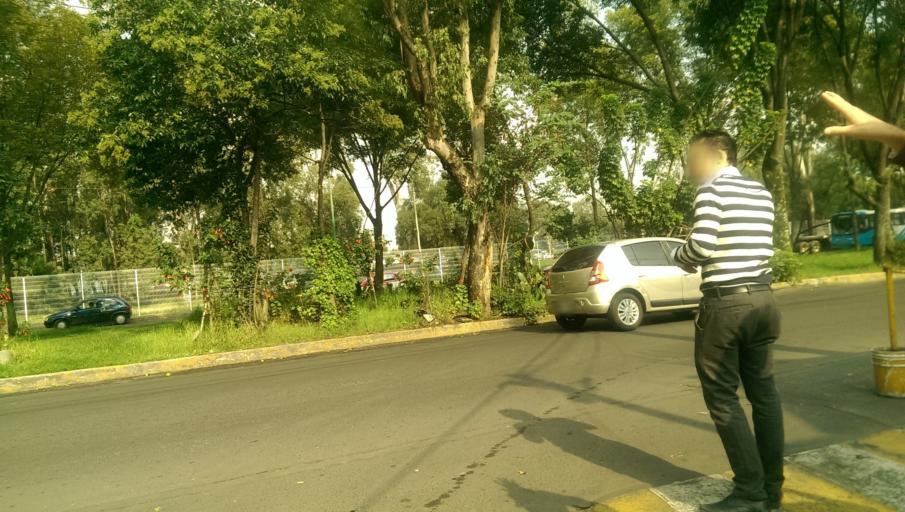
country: MX
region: Mexico City
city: Tlalpan
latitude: 19.2859
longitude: -99.1400
